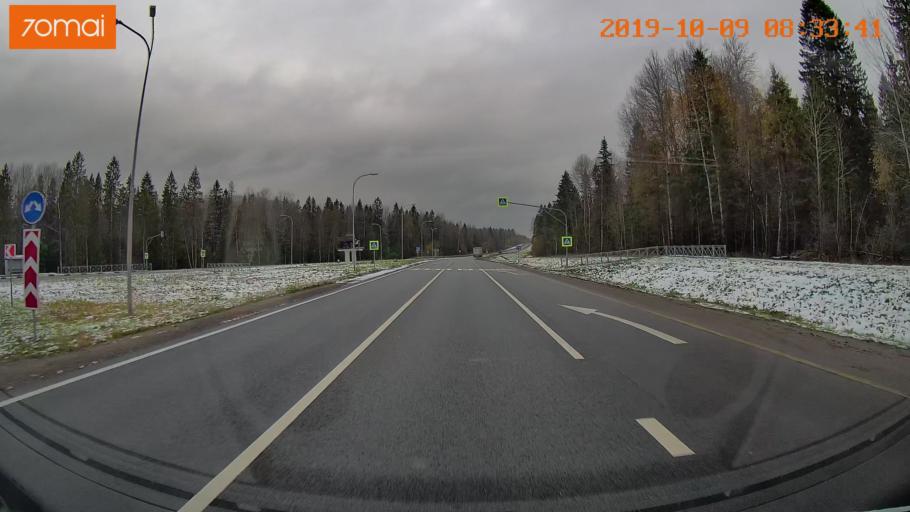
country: RU
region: Vologda
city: Gryazovets
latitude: 58.8858
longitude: 40.1911
